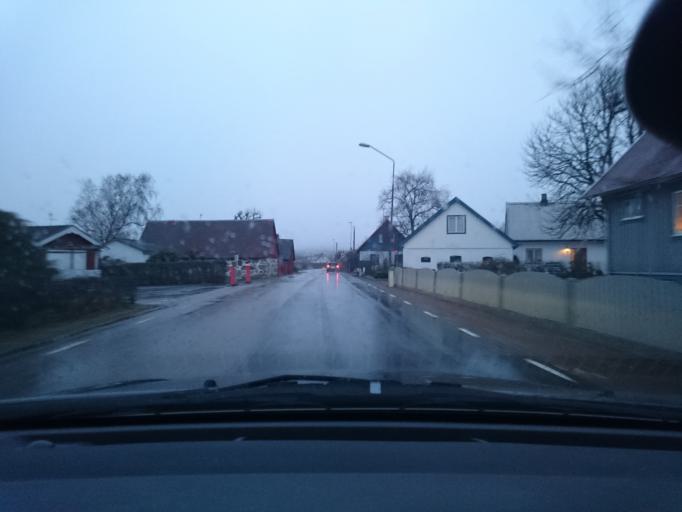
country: SE
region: Skane
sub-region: Bastads Kommun
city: Forslov
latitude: 56.3467
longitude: 12.8054
